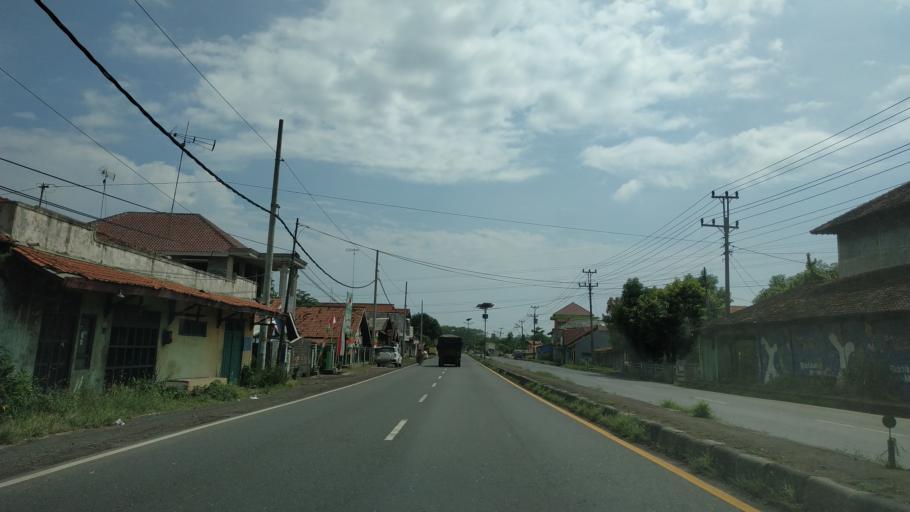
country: ID
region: Central Java
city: Pekalongan
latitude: -6.9486
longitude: 109.8086
